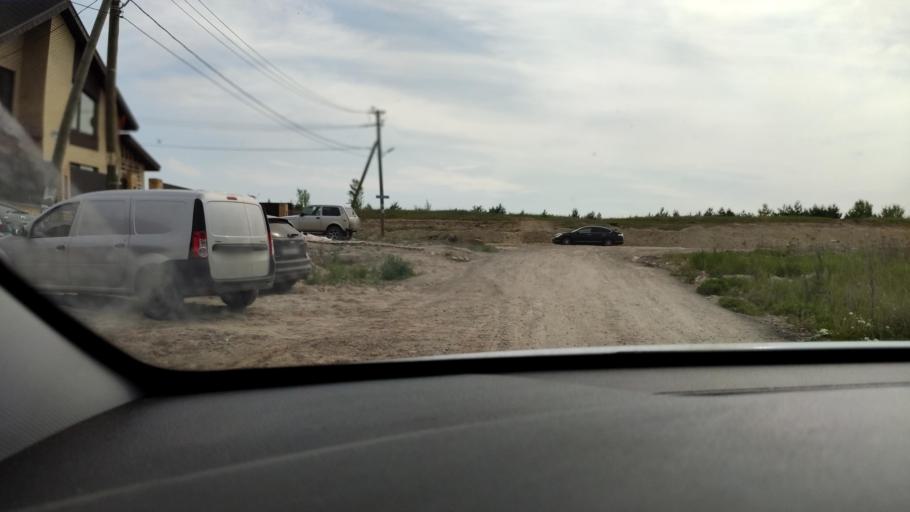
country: RU
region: Tatarstan
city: Vysokaya Gora
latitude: 55.7902
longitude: 49.2656
